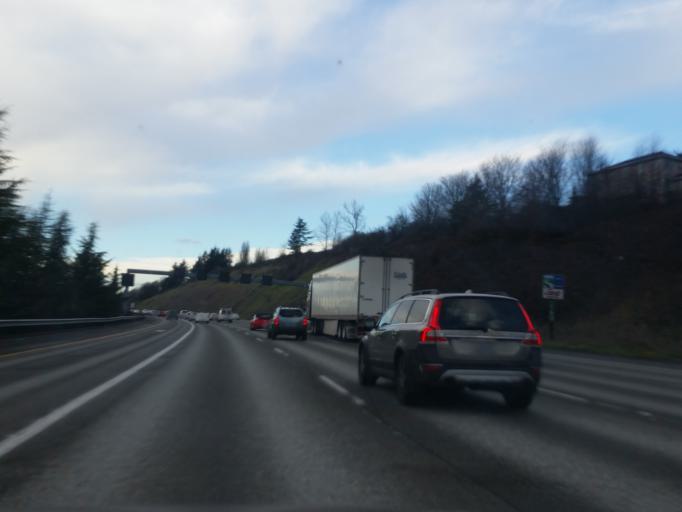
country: US
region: Washington
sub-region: King County
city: Boulevard Park
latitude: 47.5346
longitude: -122.2959
